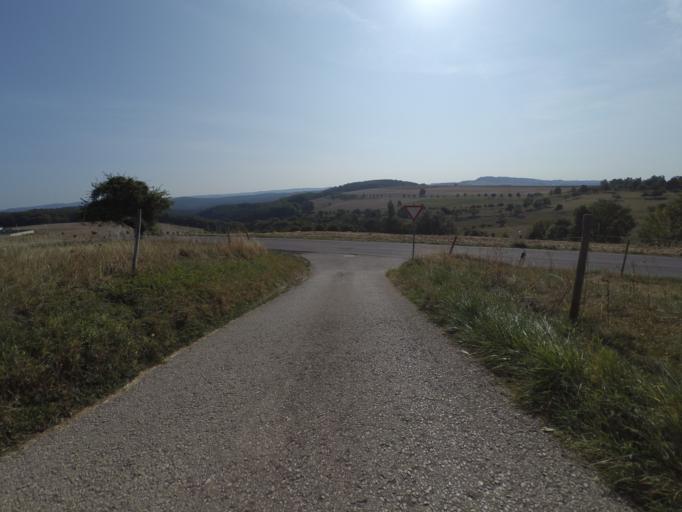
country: DE
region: Rheinland-Pfalz
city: Merzkirchen
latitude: 49.5720
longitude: 6.4919
